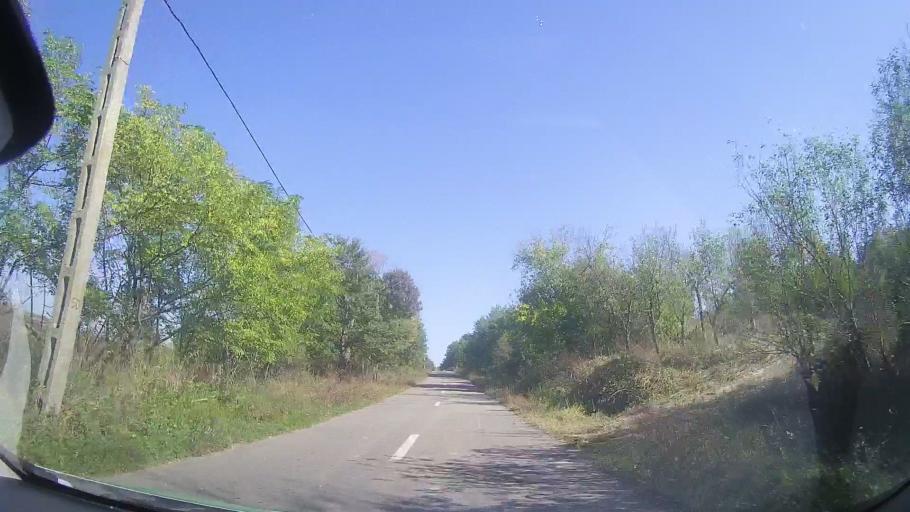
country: RO
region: Timis
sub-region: Comuna Bara
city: Bara
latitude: 45.9001
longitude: 21.8867
